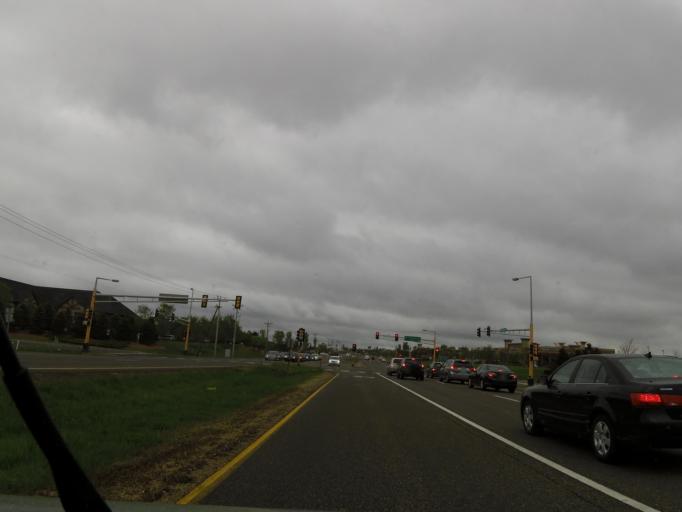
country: US
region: Minnesota
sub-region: Washington County
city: Oakdale
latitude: 44.9532
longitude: -92.9341
